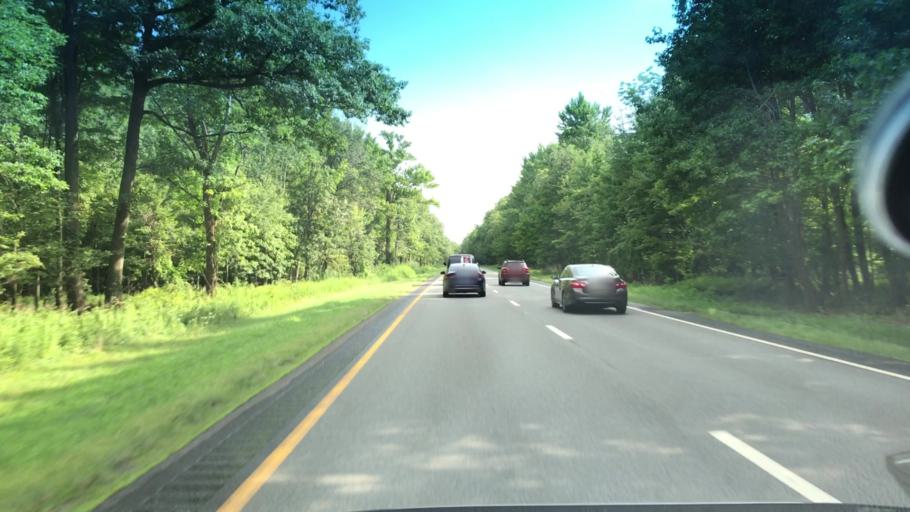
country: US
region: New Jersey
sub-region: Bergen County
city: Alpine
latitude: 40.9702
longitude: -73.9154
